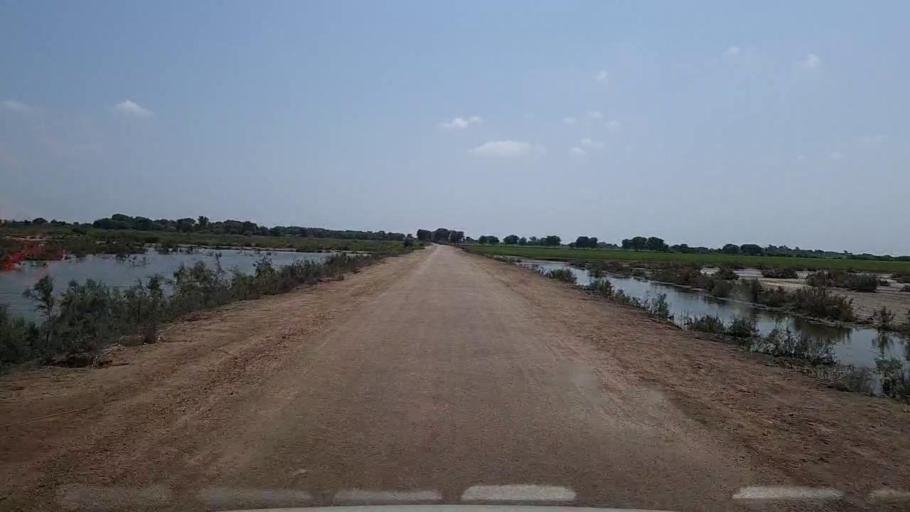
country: PK
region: Sindh
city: Kario
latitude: 24.8306
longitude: 68.7030
